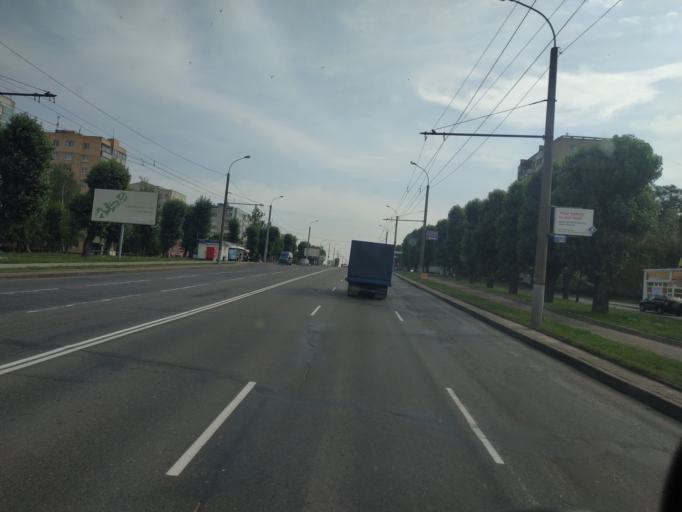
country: BY
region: Mogilev
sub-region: Mahilyowski Rayon
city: Veyno
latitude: 53.8745
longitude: 30.3761
